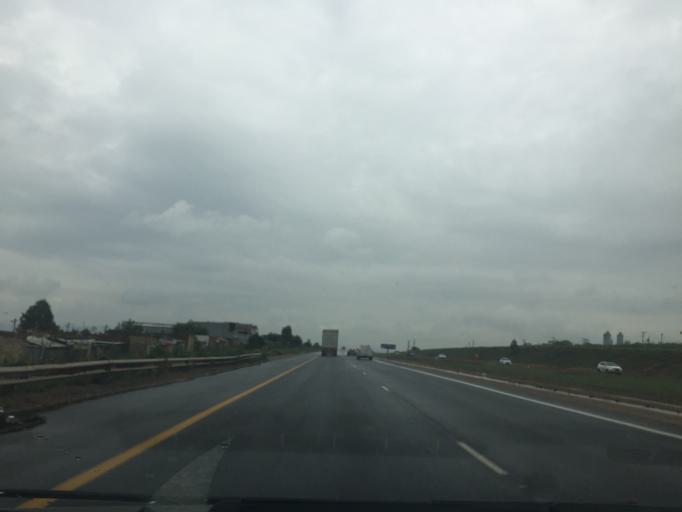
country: ZA
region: Gauteng
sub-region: City of Johannesburg Metropolitan Municipality
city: Diepsloot
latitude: -25.9223
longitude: 28.0105
